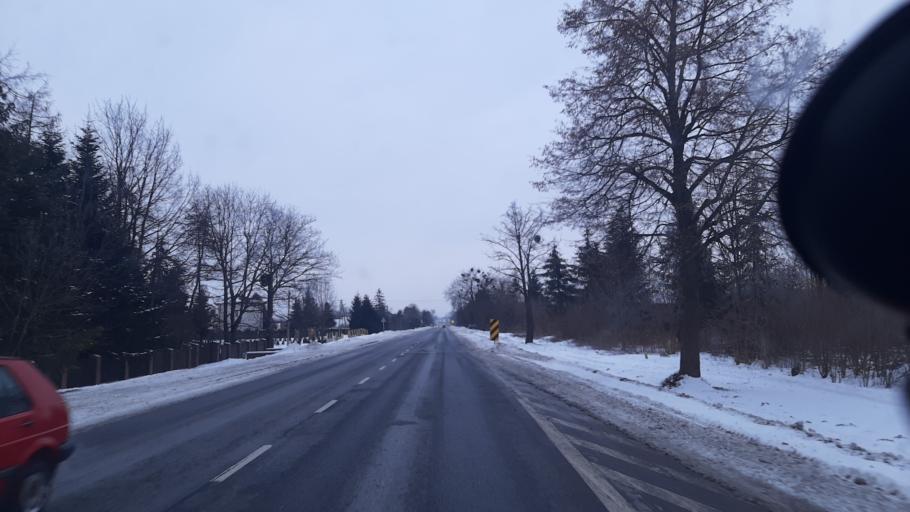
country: PL
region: Lublin Voivodeship
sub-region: Powiat pulawski
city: Markuszow
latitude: 51.3770
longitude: 22.2481
